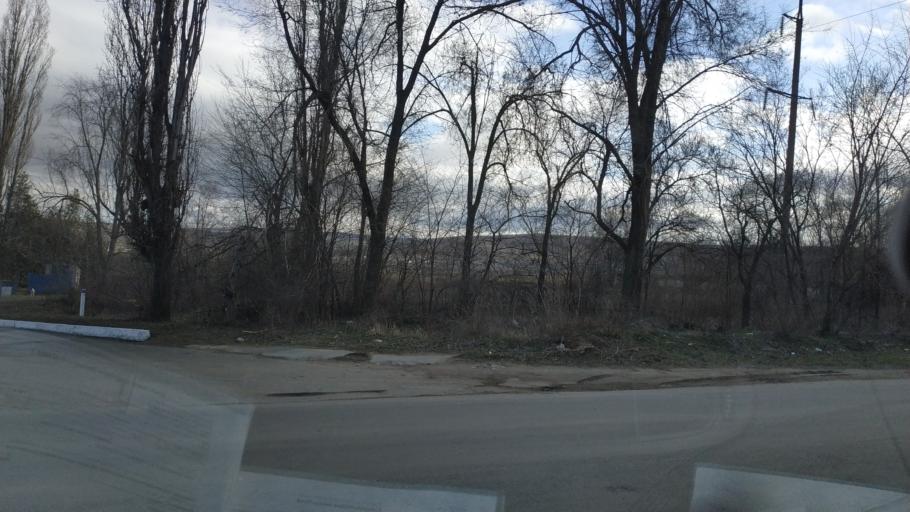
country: MD
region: Causeni
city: Causeni
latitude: 46.6605
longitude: 29.4232
